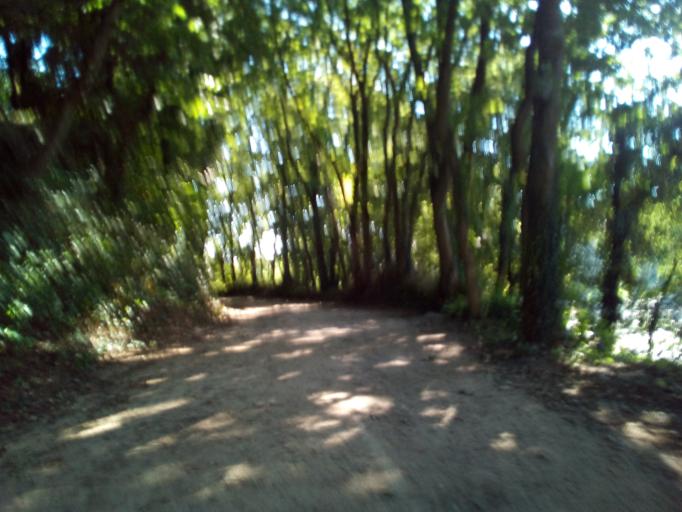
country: FR
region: Brittany
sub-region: Departement du Finistere
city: Landivisiau
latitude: 48.5077
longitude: -4.0790
